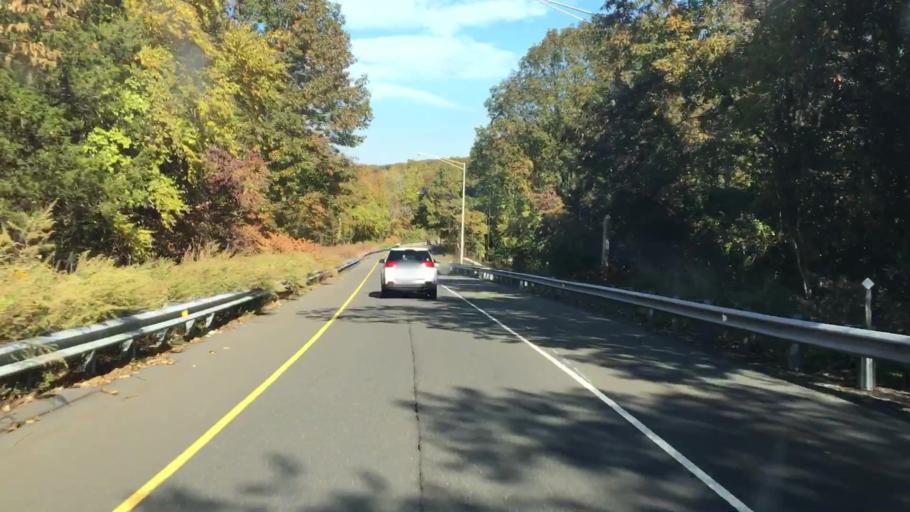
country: US
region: Connecticut
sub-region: Fairfield County
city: Trumbull
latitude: 41.2339
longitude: -73.1857
